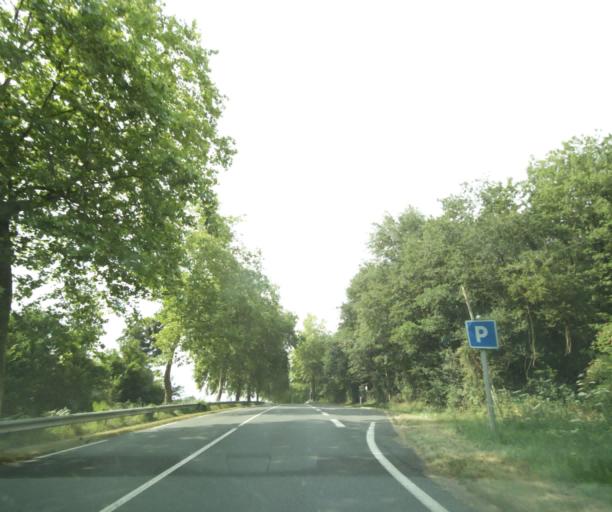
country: FR
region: Centre
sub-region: Departement d'Indre-et-Loire
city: Saint-Paterne-Racan
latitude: 47.6142
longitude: 0.5076
